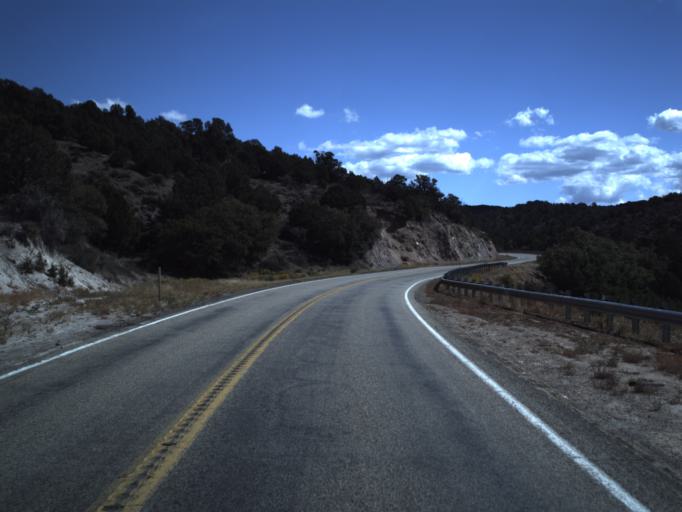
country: US
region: Utah
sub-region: Washington County
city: Enterprise
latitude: 37.5410
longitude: -113.6765
